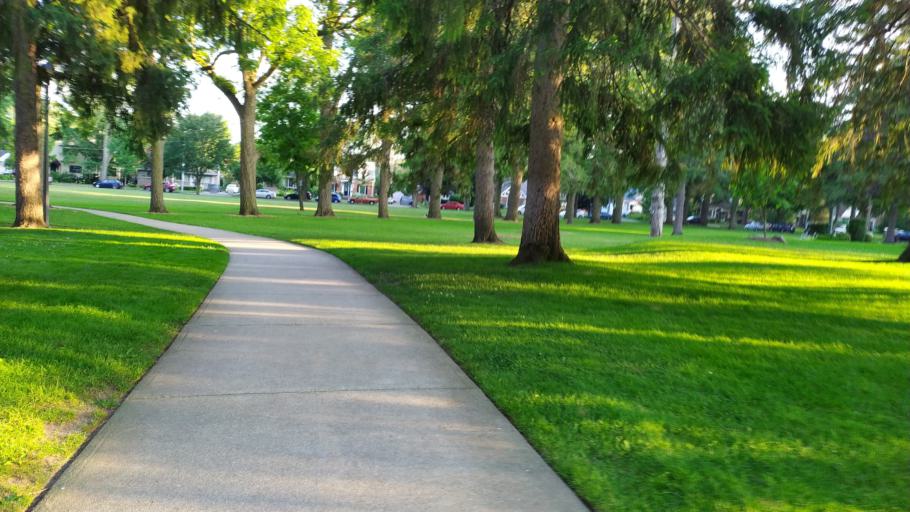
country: CA
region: Ontario
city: Stratford
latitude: 43.3738
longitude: -80.9679
